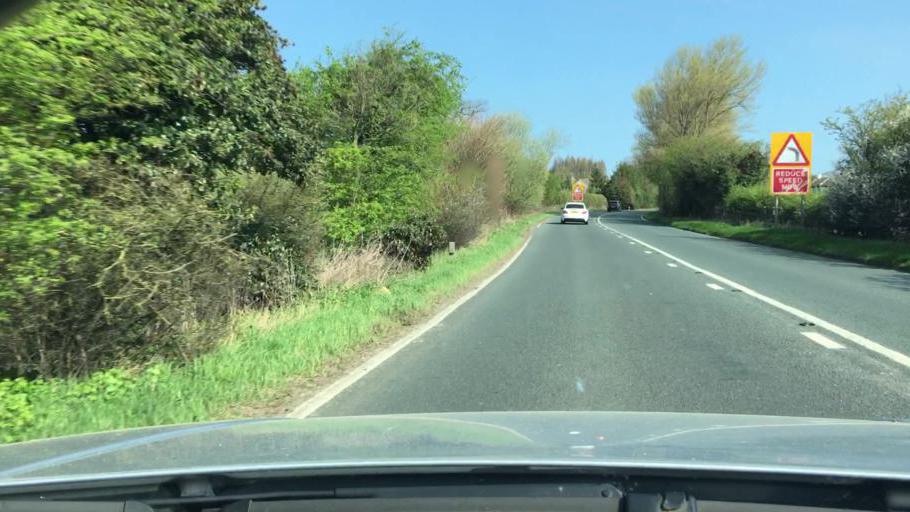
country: GB
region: England
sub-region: North Yorkshire
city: Pannal
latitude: 53.9361
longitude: -1.5369
